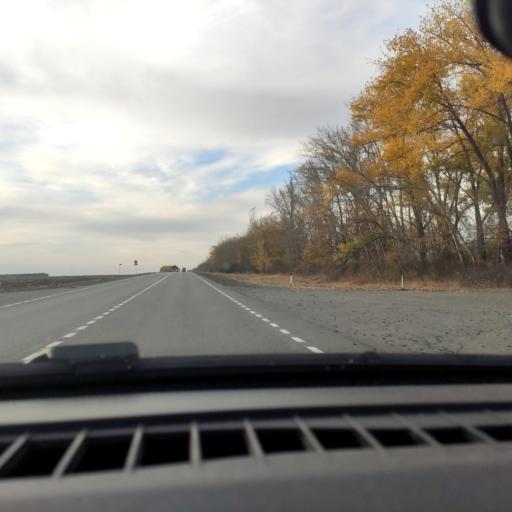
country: RU
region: Voronezj
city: Ostrogozhsk
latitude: 50.9495
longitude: 39.0500
